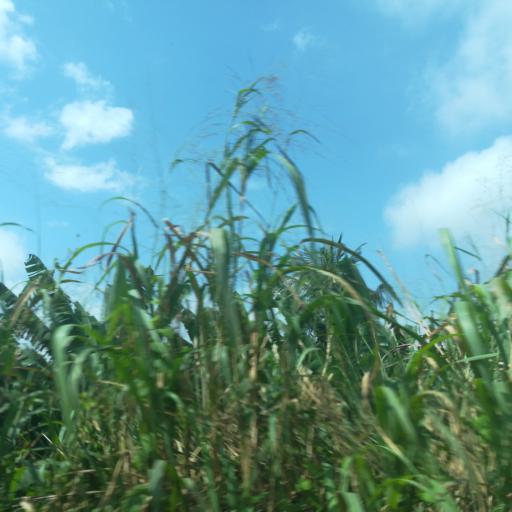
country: NG
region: Lagos
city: Ikorodu
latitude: 6.6622
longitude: 3.6785
